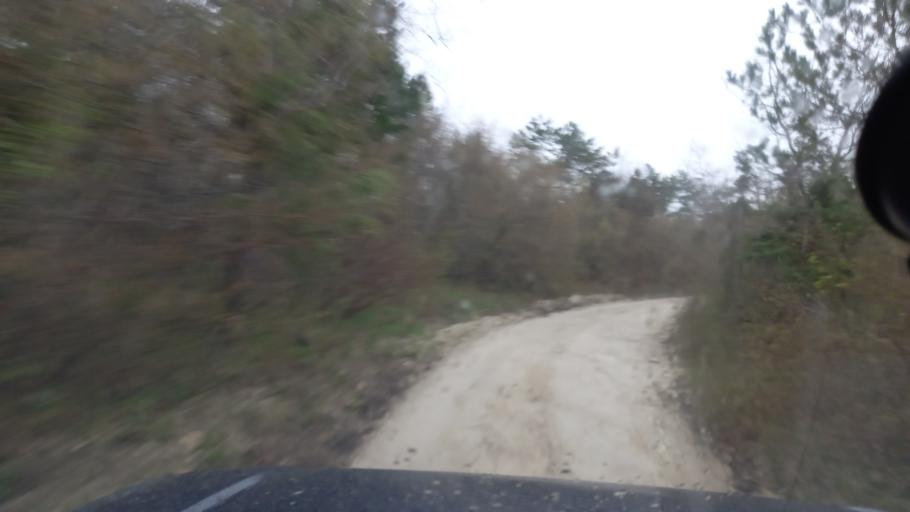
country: RU
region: Krasnodarskiy
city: Dzhubga
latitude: 44.3227
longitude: 38.6879
